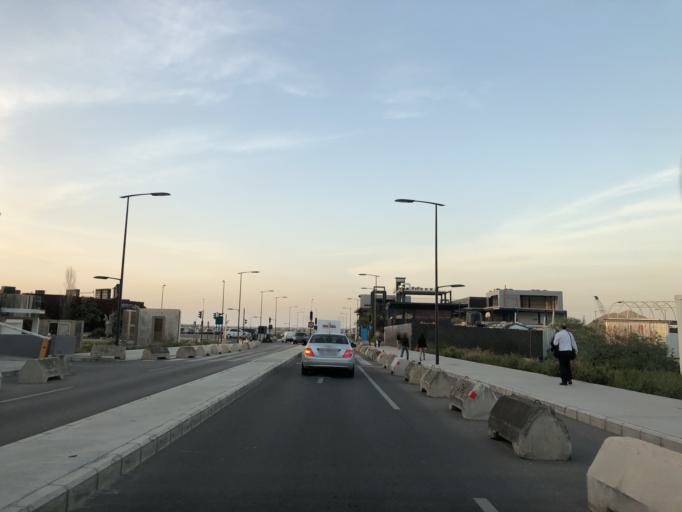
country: LB
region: Beyrouth
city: Beirut
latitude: 33.9047
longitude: 35.5060
